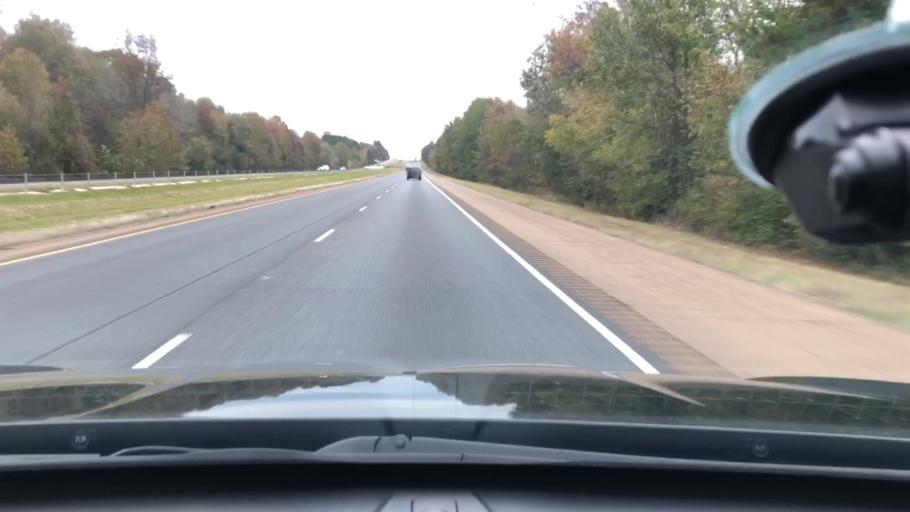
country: US
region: Arkansas
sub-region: Clark County
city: Gurdon
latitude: 33.9831
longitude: -93.1973
